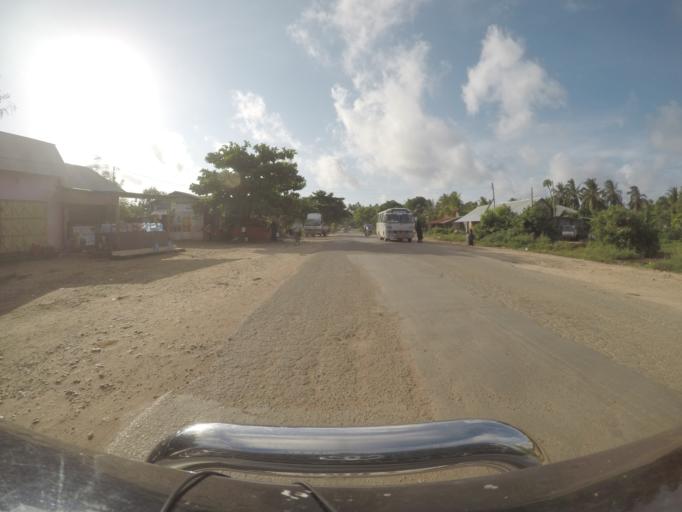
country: TZ
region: Zanzibar Central/South
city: Koani
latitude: -6.1951
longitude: 39.3036
